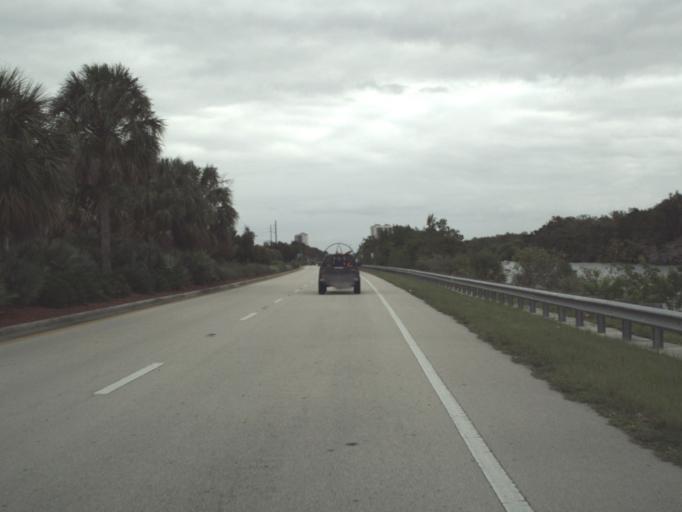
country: US
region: Florida
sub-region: Collier County
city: Marco
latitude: 25.9760
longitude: -81.7053
